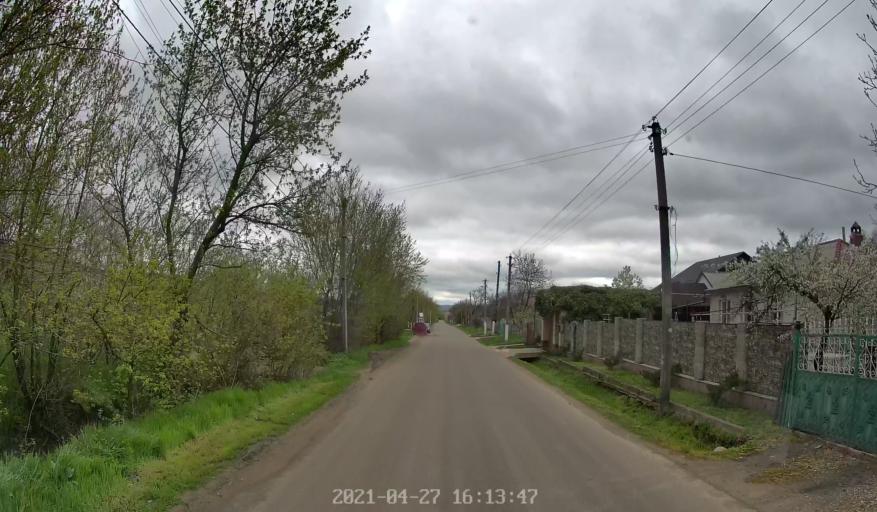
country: MD
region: Chisinau
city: Singera
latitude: 47.0069
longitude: 29.0135
